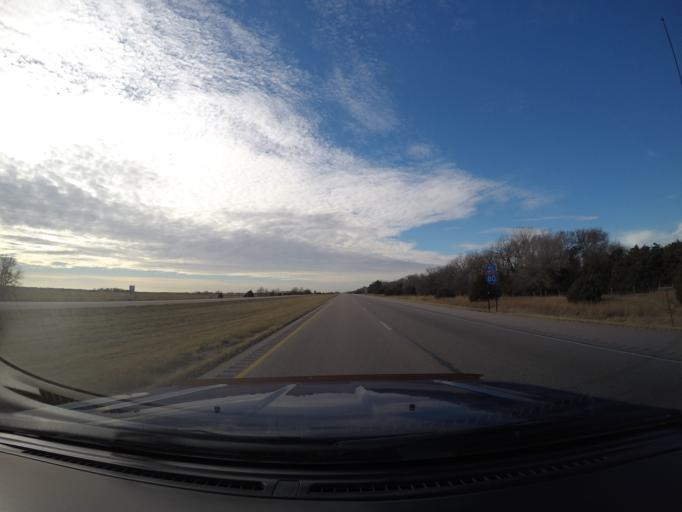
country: US
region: Nebraska
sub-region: Hall County
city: Grand Island
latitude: 40.8212
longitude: -98.2694
